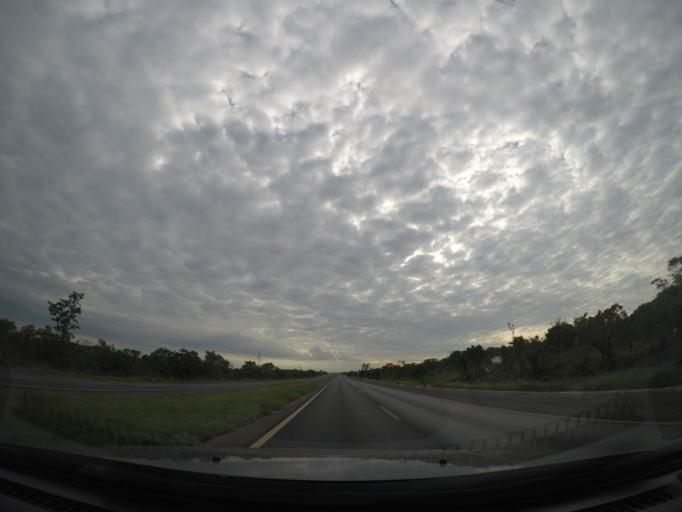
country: BR
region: Goias
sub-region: Planaltina
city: Planaltina
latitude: -15.5968
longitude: -47.6361
